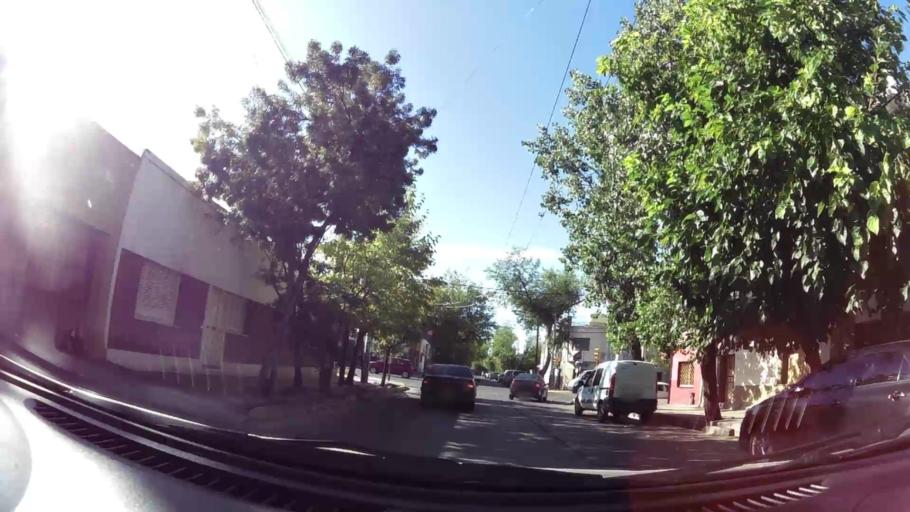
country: AR
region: Mendoza
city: Mendoza
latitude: -32.9004
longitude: -68.8305
